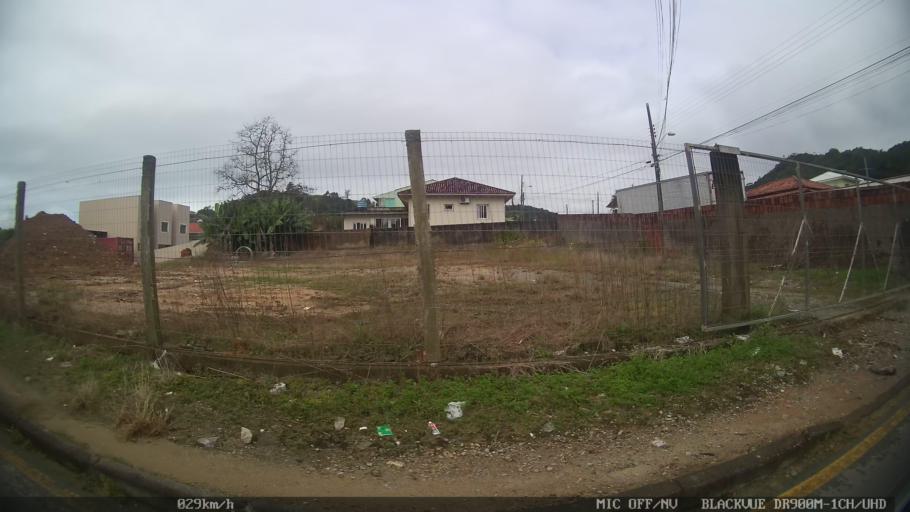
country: BR
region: Santa Catarina
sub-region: Biguacu
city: Biguacu
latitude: -27.5456
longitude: -48.6455
